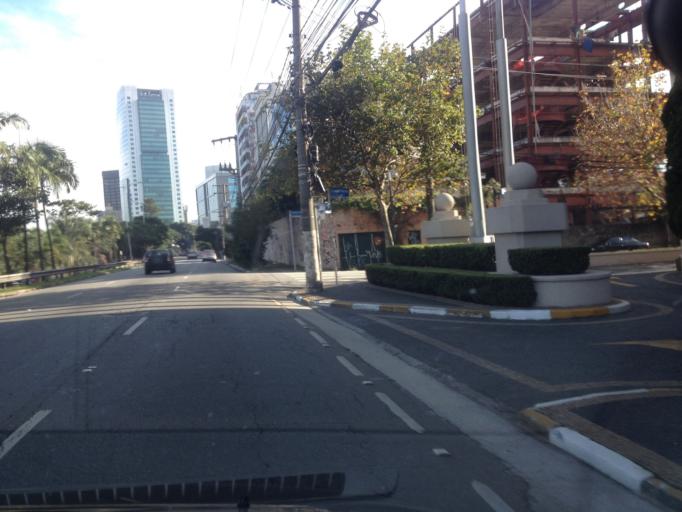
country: BR
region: Sao Paulo
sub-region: Sao Paulo
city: Sao Paulo
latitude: -23.5779
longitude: -46.6946
